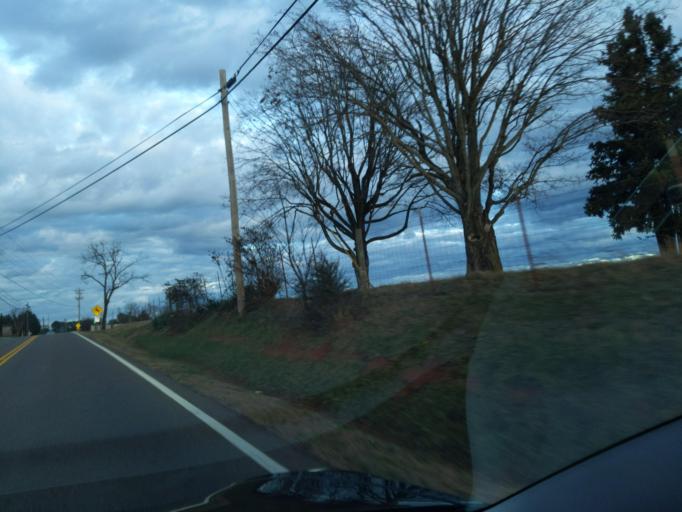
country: US
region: Tennessee
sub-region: Jefferson County
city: Dandridge
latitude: 35.9885
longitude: -83.4552
